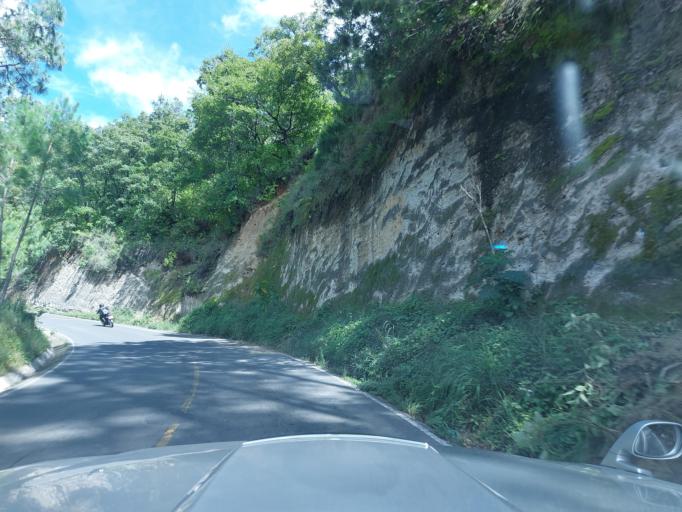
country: GT
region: Chimaltenango
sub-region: Municipio de Santa Cruz Balanya
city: Santa Cruz Balanya
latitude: 14.6964
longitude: -90.8967
